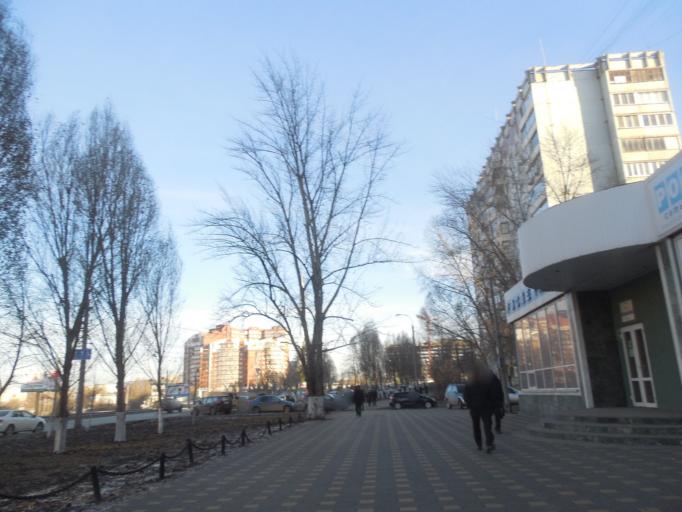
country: RU
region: Samara
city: Samara
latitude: 53.2109
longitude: 50.1427
